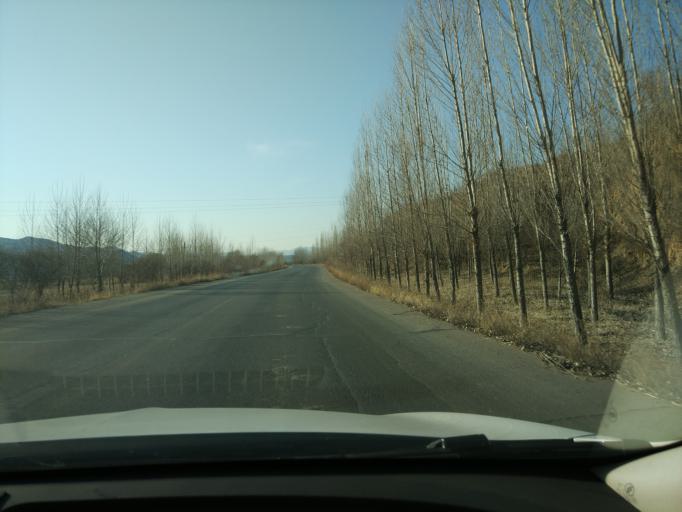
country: CN
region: Hebei
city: Chicheng
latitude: 40.7251
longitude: 115.7972
